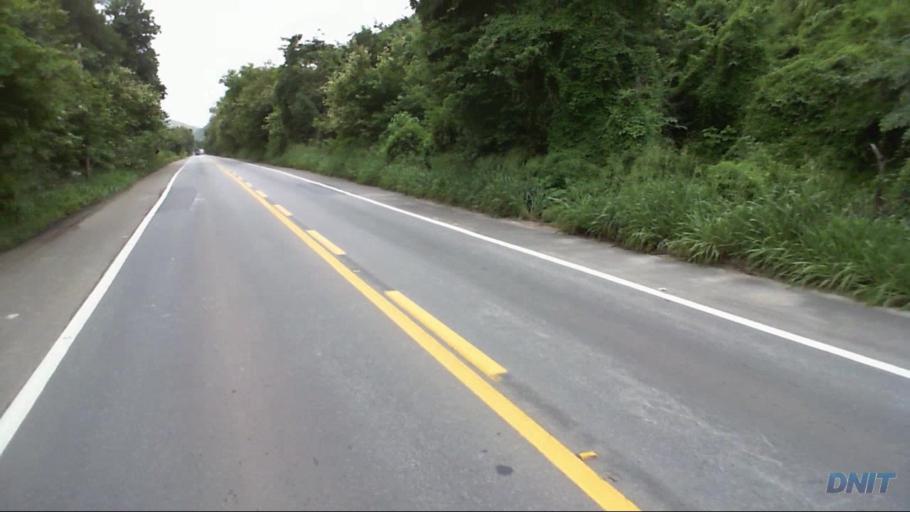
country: BR
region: Minas Gerais
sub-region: Timoteo
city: Timoteo
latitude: -19.5534
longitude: -42.7085
